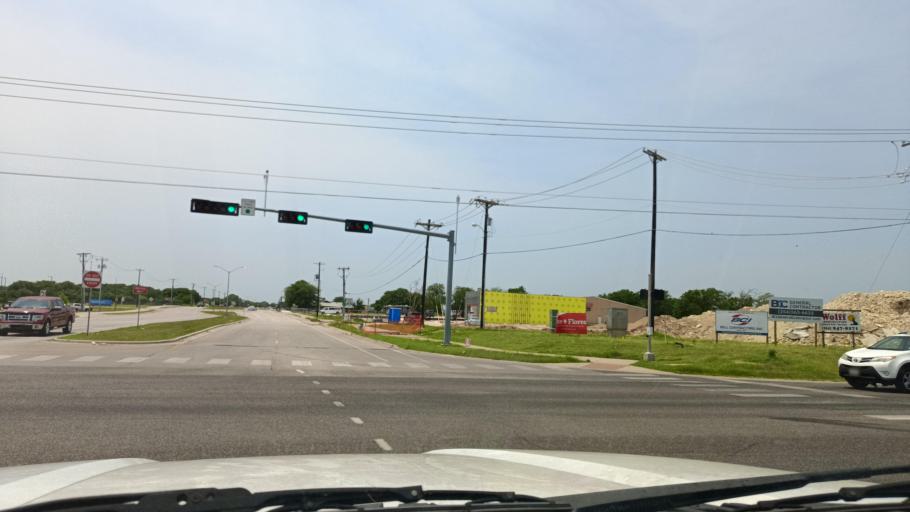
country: US
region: Texas
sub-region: Bell County
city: Morgans Point Resort
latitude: 31.1177
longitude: -97.4162
